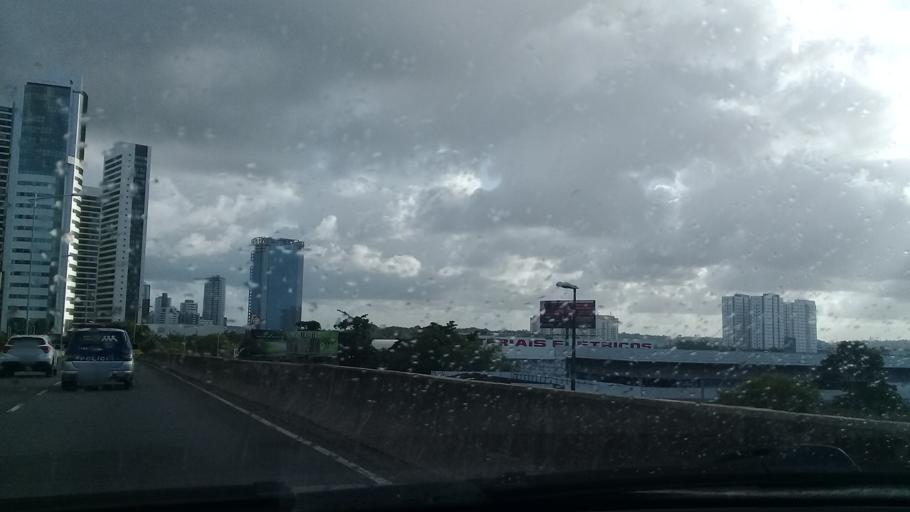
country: BR
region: Pernambuco
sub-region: Recife
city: Recife
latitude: -8.1132
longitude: -34.9024
